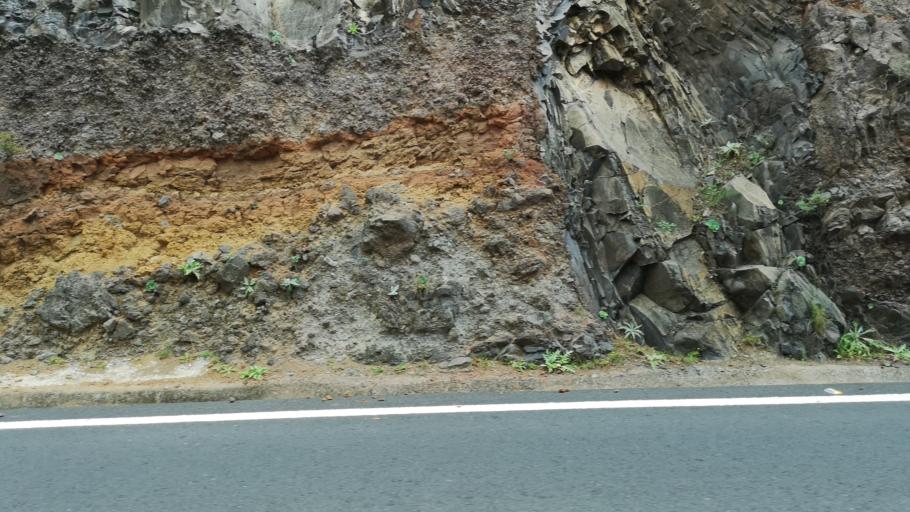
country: ES
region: Canary Islands
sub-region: Provincia de Santa Cruz de Tenerife
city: Vallehermosa
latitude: 28.1189
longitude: -17.3184
